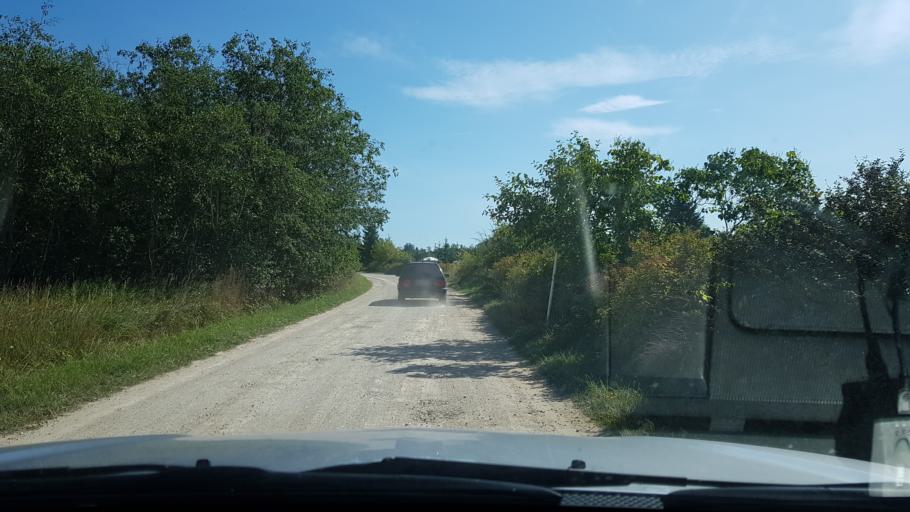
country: EE
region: Ida-Virumaa
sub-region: Sillamaee linn
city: Sillamae
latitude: 59.3730
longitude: 27.7872
